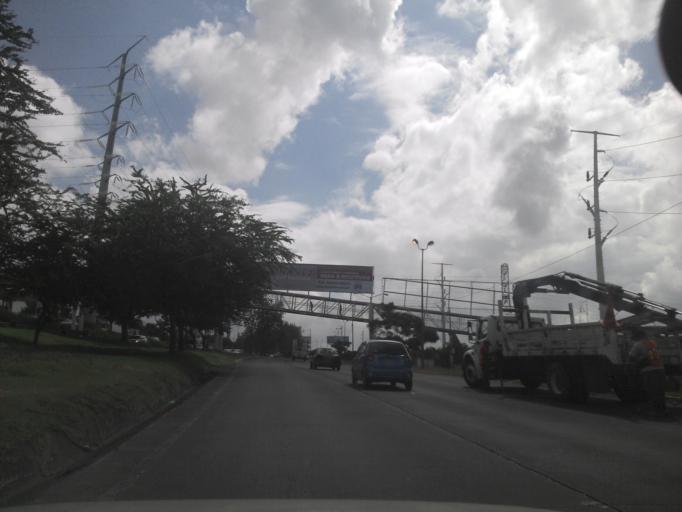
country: MX
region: Jalisco
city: Tlaquepaque
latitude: 20.6236
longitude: -103.3156
